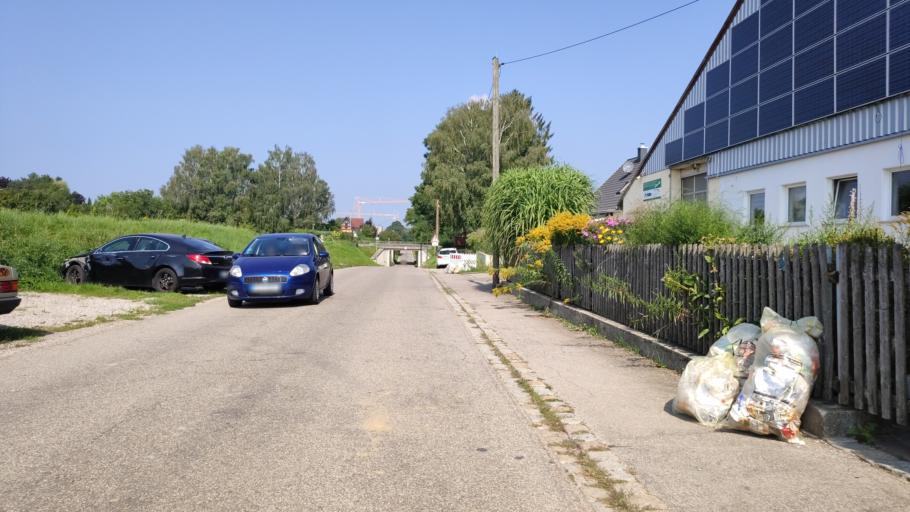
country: DE
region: Bavaria
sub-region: Swabia
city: Bobingen
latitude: 48.2605
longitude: 10.8357
